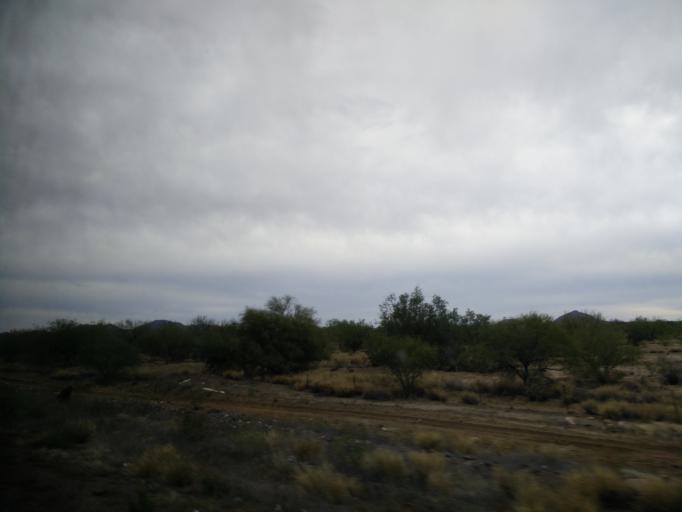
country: MX
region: Sonora
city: Hermosillo
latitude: 28.7308
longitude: -110.9783
